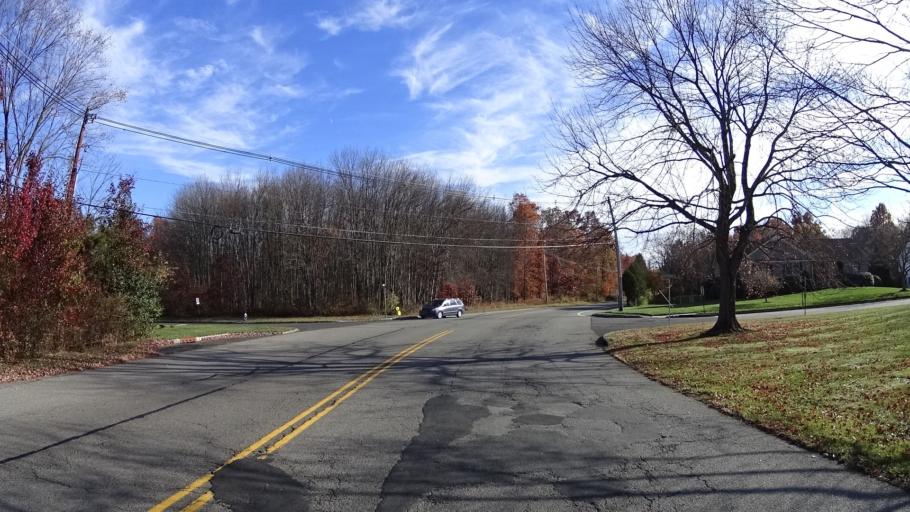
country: US
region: New Jersey
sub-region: Union County
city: Berkeley Heights
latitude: 40.6819
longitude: -74.4686
